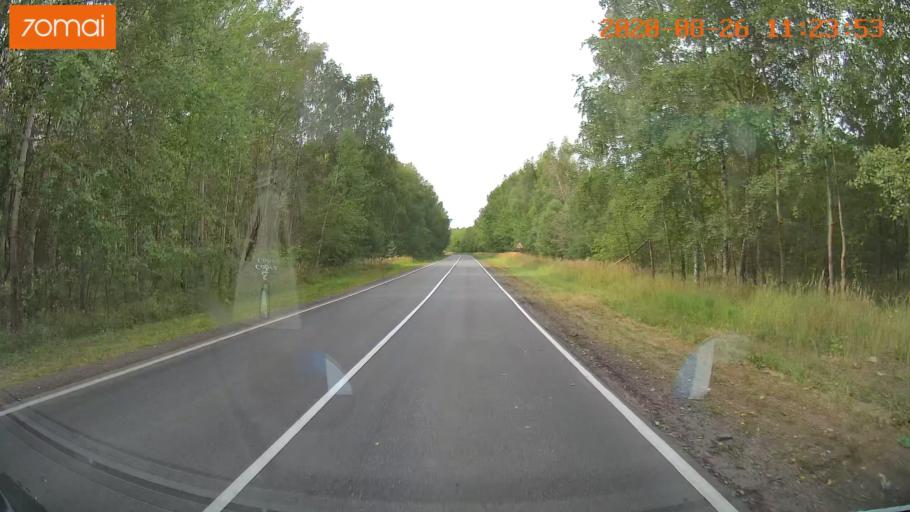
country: RU
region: Rjazan
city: Shilovo
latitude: 54.3493
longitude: 41.0008
